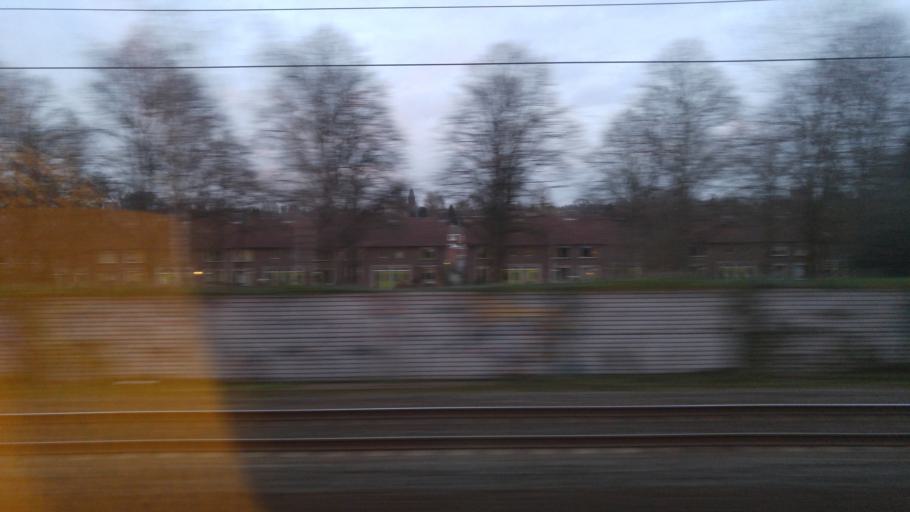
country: NL
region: North Brabant
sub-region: Gemeente Eindhoven
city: Eindhoven
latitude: 51.4539
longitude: 5.4522
